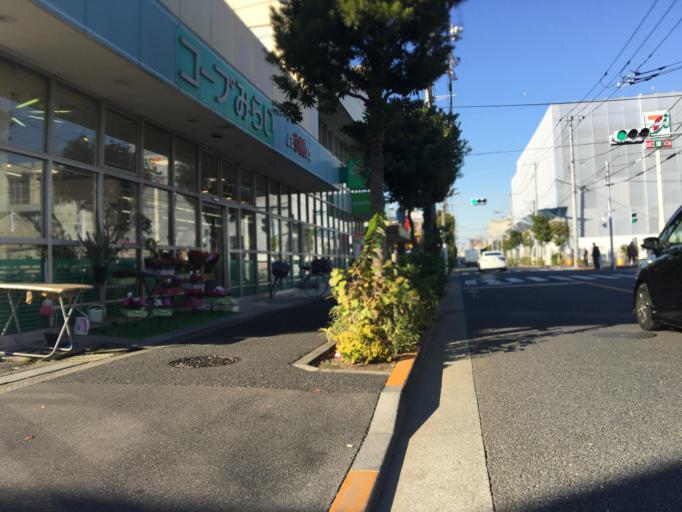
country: JP
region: Tokyo
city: Urayasu
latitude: 35.7201
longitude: 139.8907
